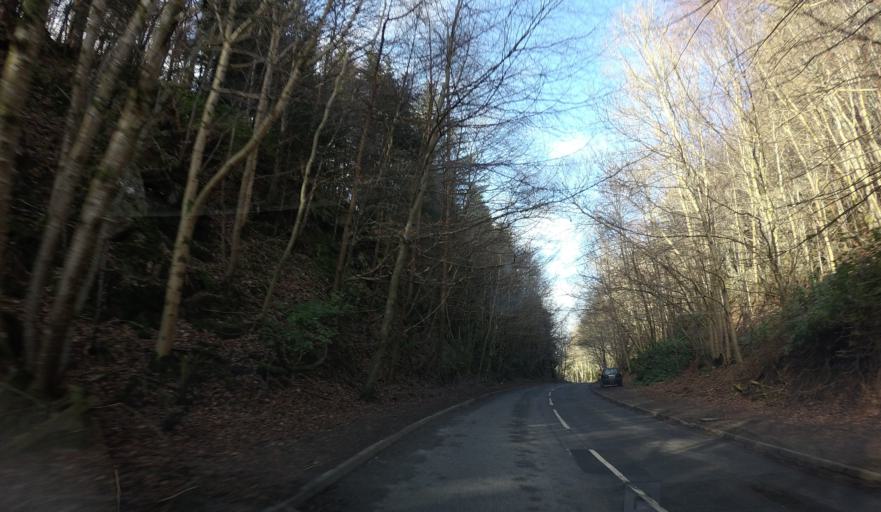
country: GB
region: Scotland
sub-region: Perth and Kinross
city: Bankfoot
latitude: 56.5692
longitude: -3.6129
